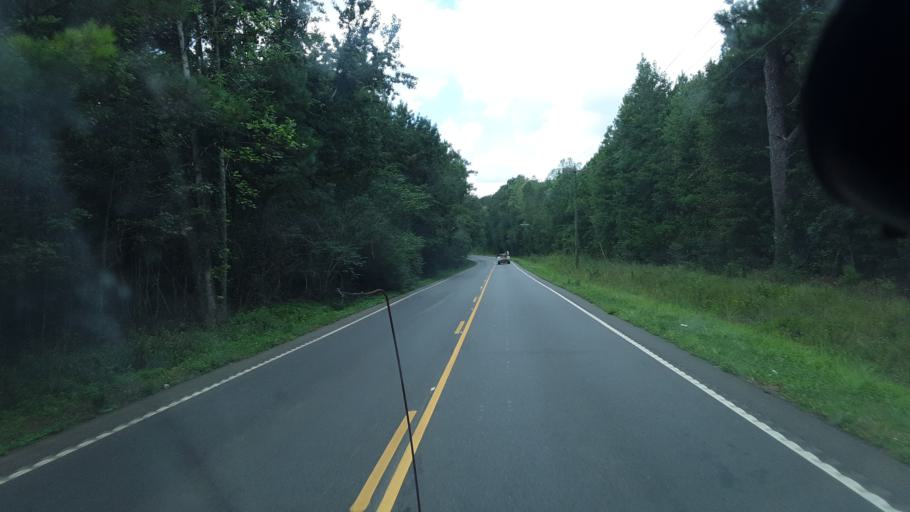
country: US
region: South Carolina
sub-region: Williamsburg County
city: Andrews
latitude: 33.3608
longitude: -79.4720
